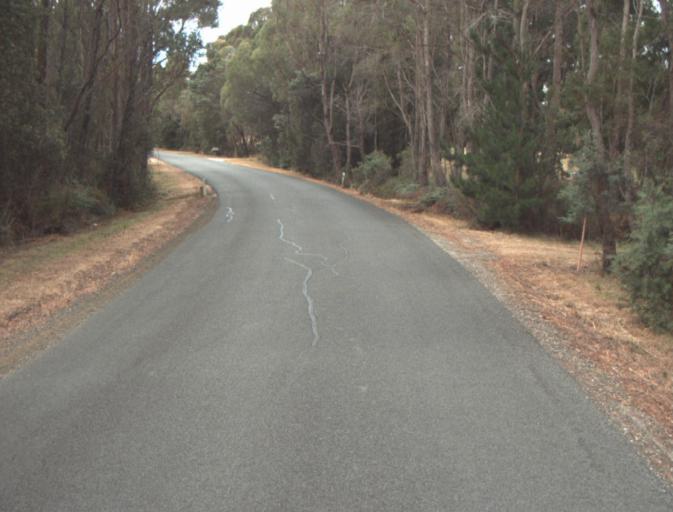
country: AU
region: Tasmania
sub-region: Launceston
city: Mayfield
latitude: -41.2221
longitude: 147.0467
